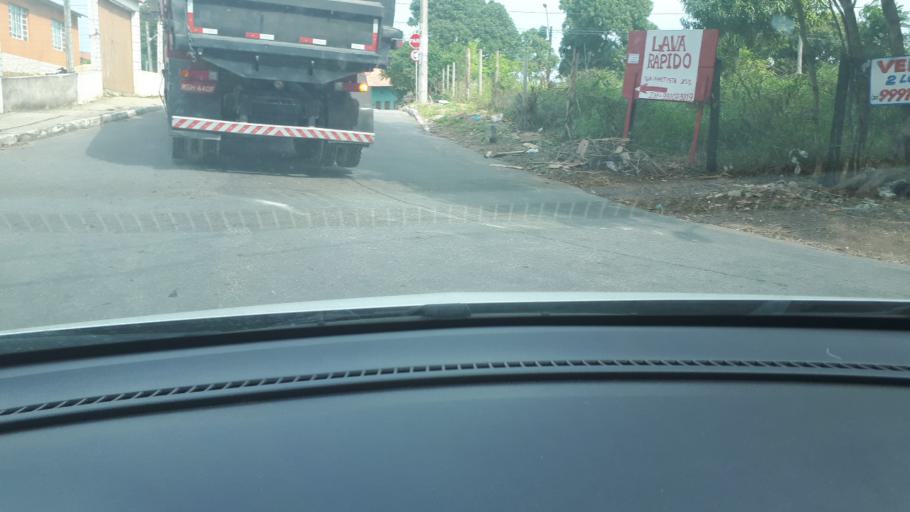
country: BR
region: Espirito Santo
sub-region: Serra
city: Serra
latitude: -20.1471
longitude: -40.1982
